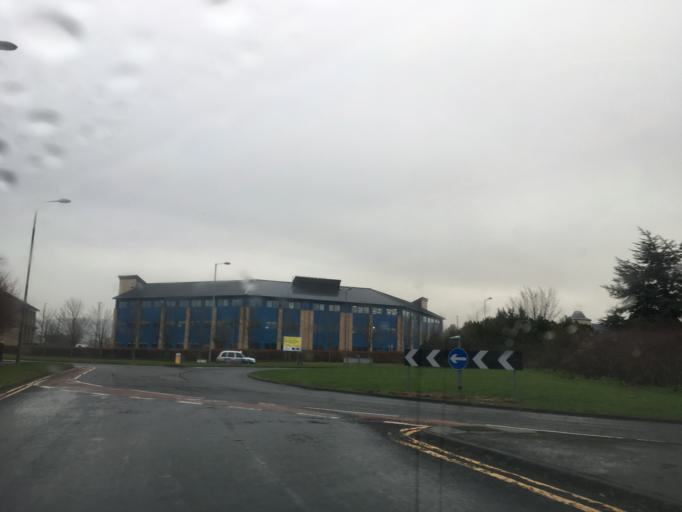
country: GB
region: Scotland
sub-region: Edinburgh
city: Currie
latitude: 55.9353
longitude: -3.3069
